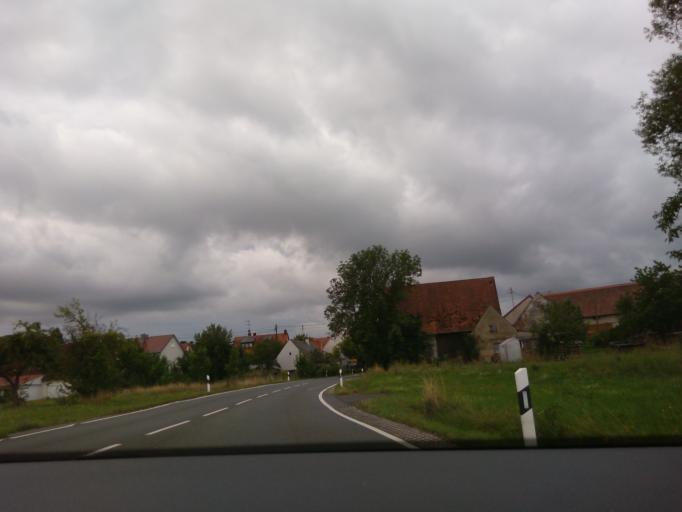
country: DE
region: Bavaria
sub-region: Regierungsbezirk Mittelfranken
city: Weisendorf
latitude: 49.6358
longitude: 10.8191
